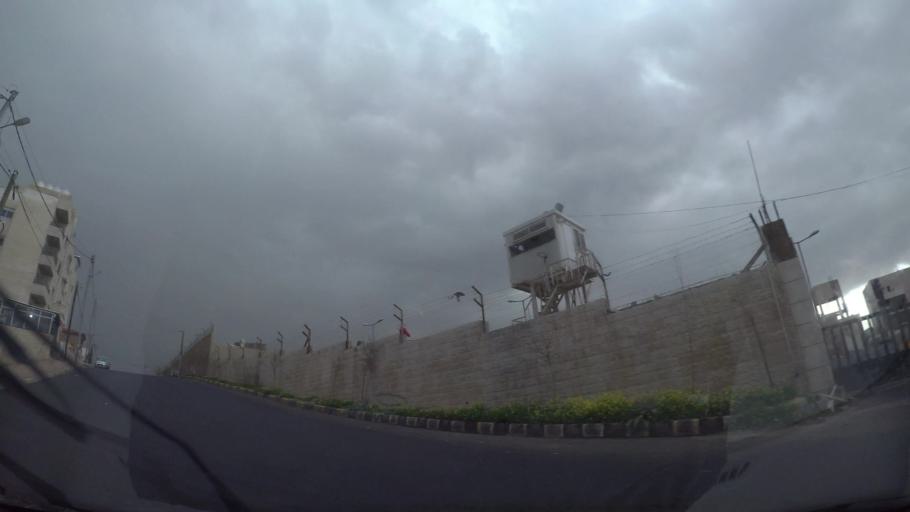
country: JO
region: Amman
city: Amman
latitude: 32.0101
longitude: 35.9573
